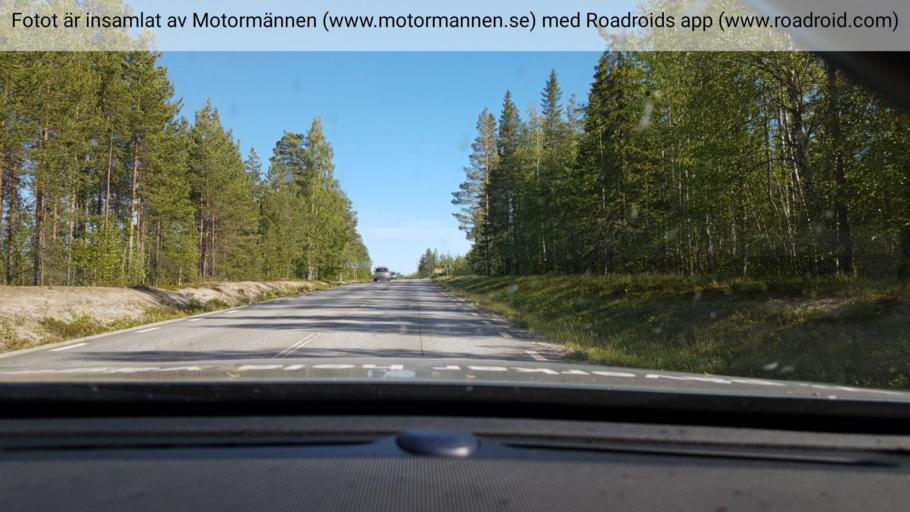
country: SE
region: Vaesterbotten
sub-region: Lycksele Kommun
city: Lycksele
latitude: 64.6284
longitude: 18.6245
